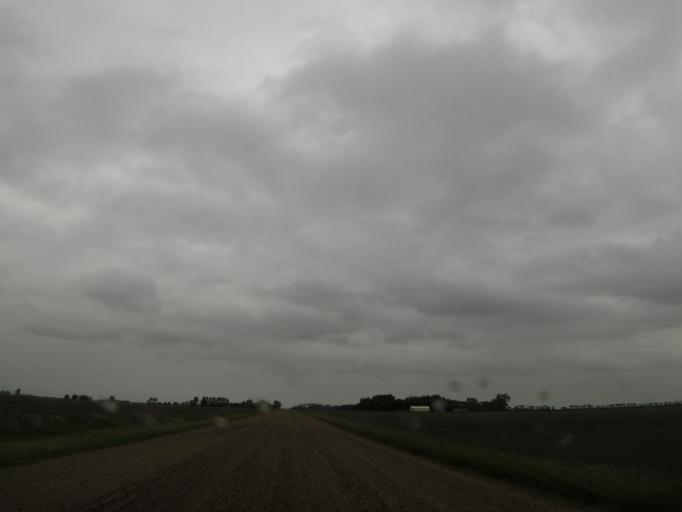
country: US
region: North Dakota
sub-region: Walsh County
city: Grafton
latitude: 48.5228
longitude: -97.2997
